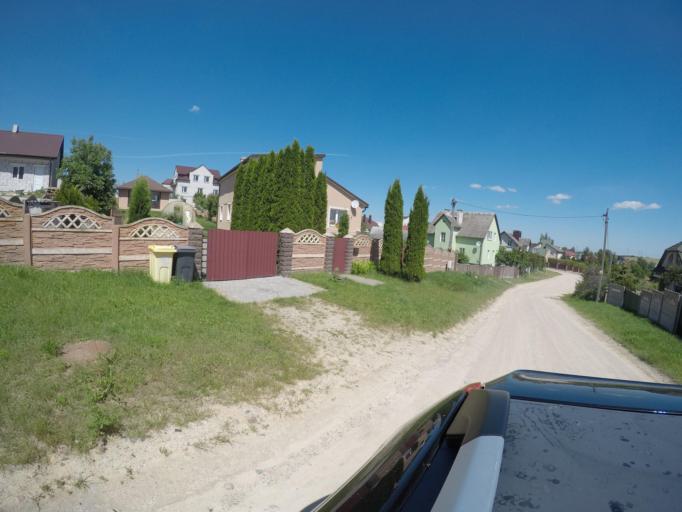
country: BY
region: Grodnenskaya
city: Hrodna
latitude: 53.7210
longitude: 23.8514
